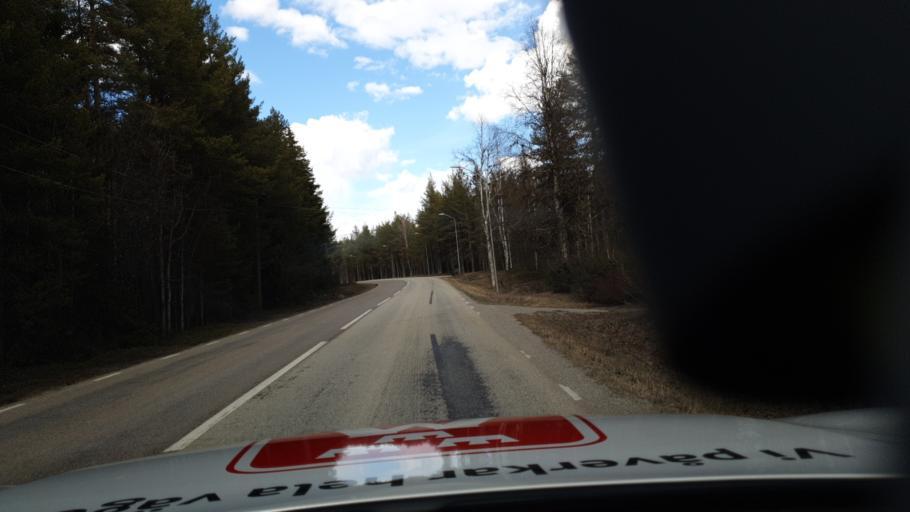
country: SE
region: Jaemtland
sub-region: Harjedalens Kommun
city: Sveg
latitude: 62.4383
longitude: 13.8458
